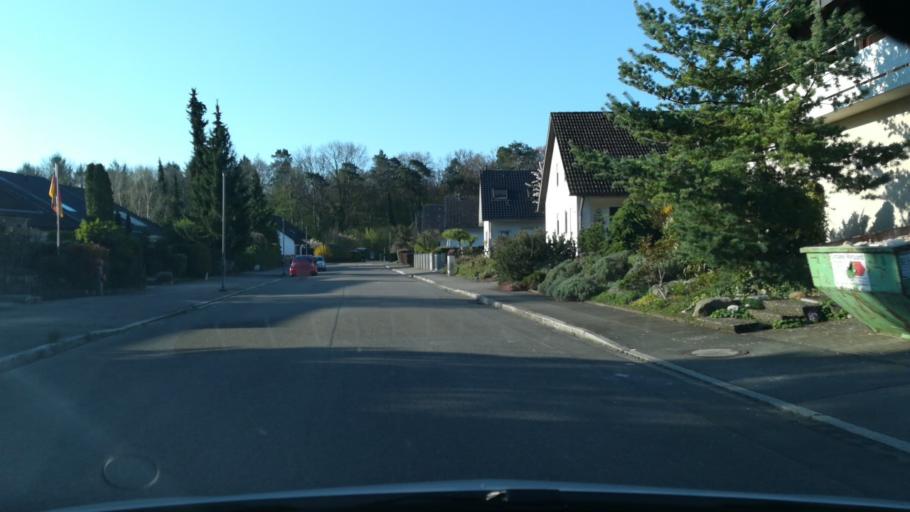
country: DE
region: Baden-Wuerttemberg
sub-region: Freiburg Region
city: Singen
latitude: 47.7761
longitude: 8.8506
